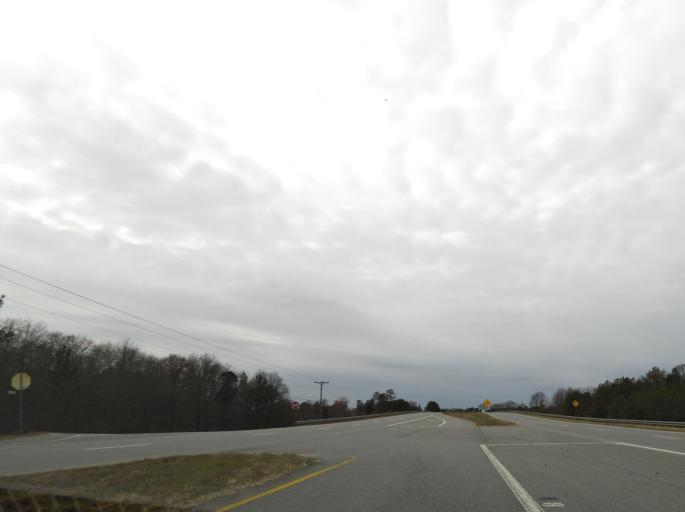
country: US
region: Georgia
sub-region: Peach County
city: Byron
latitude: 32.6364
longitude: -83.7714
